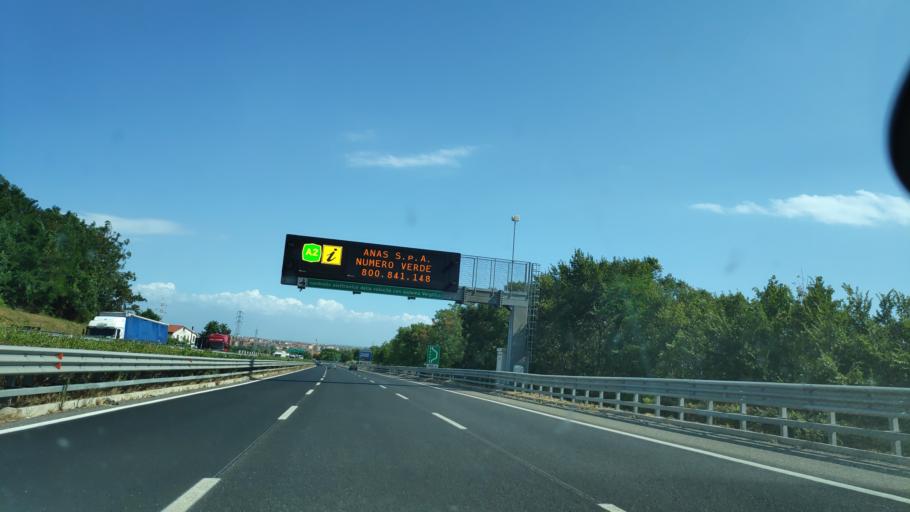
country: IT
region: Campania
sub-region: Provincia di Salerno
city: Fuorni
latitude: 40.6609
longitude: 14.8601
